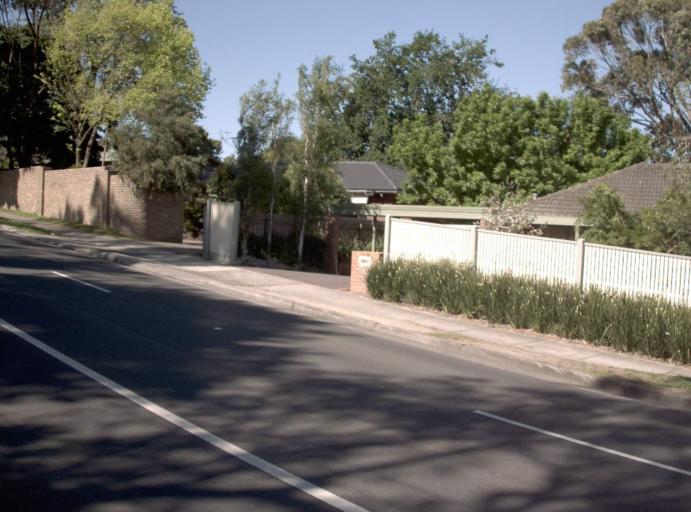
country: AU
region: Victoria
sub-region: Knox
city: Bayswater
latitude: -37.8629
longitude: 145.2658
